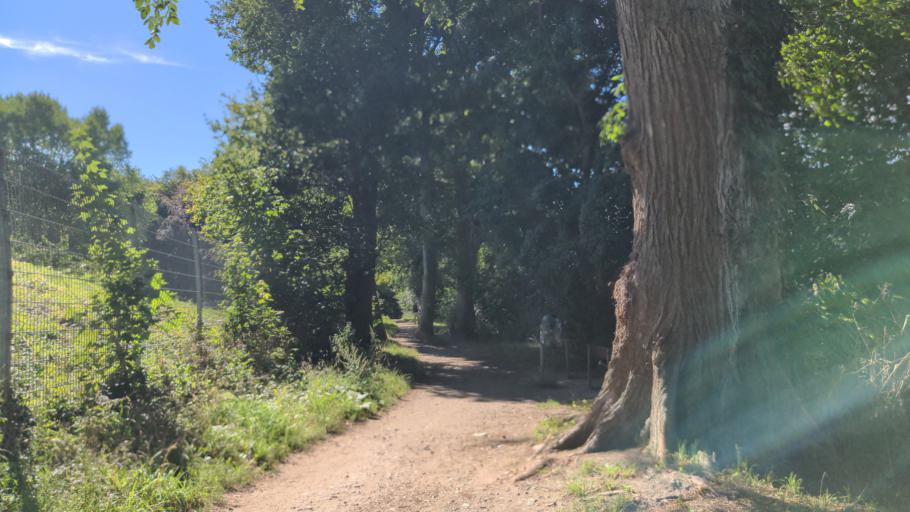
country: DE
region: Schleswig-Holstein
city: Lensahn
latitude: 54.2144
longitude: 10.8762
